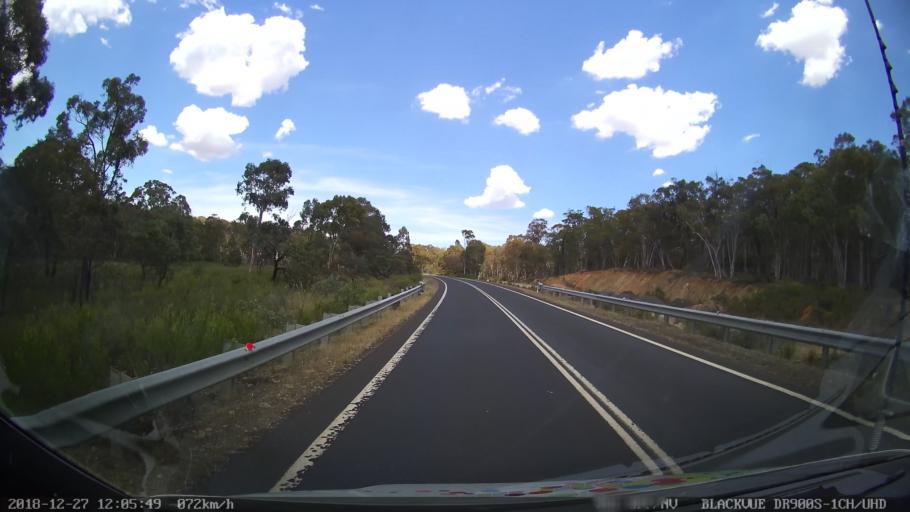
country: AU
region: New South Wales
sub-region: Blayney
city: Blayney
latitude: -33.8040
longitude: 149.3342
